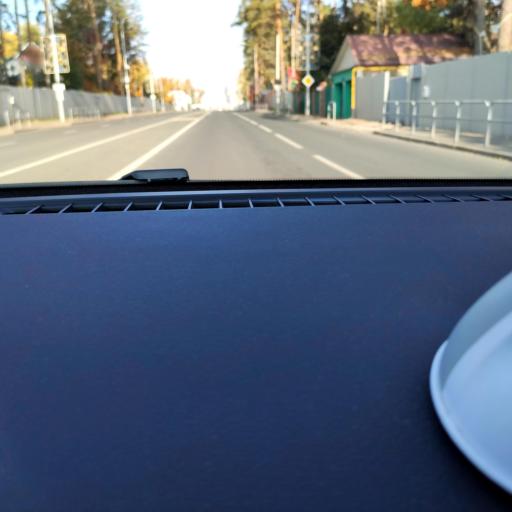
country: RU
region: Samara
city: Samara
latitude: 53.2650
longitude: 50.2432
